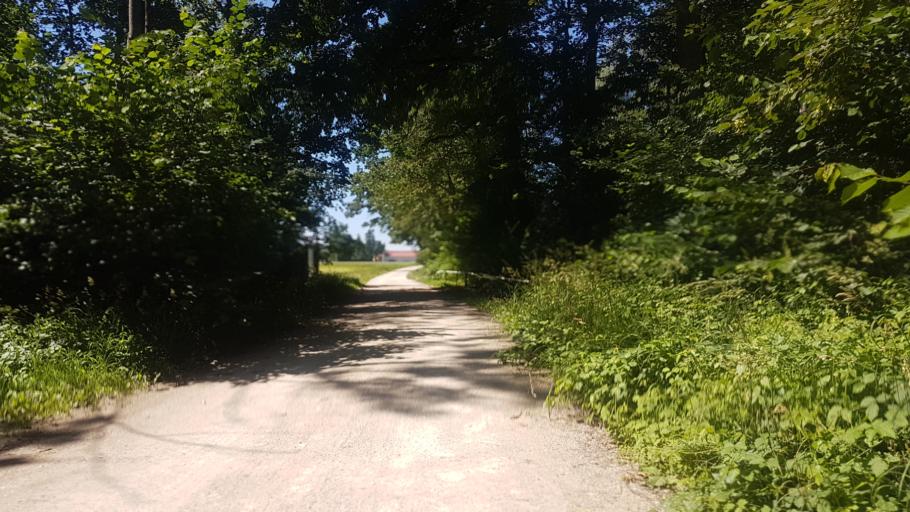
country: DE
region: Bavaria
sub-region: Upper Bavaria
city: Weichering
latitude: 48.7271
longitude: 11.3131
